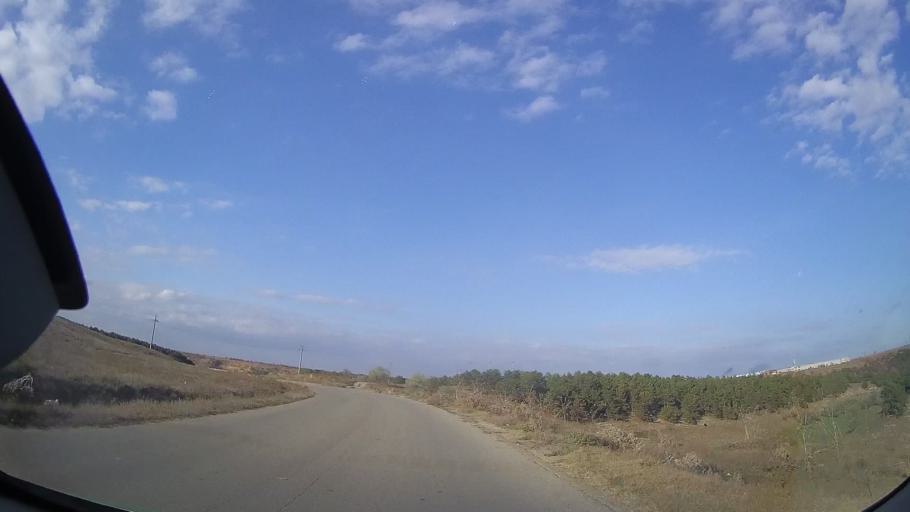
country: RO
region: Constanta
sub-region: Comuna Limanu
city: Limanu
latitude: 43.8085
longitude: 28.5200
